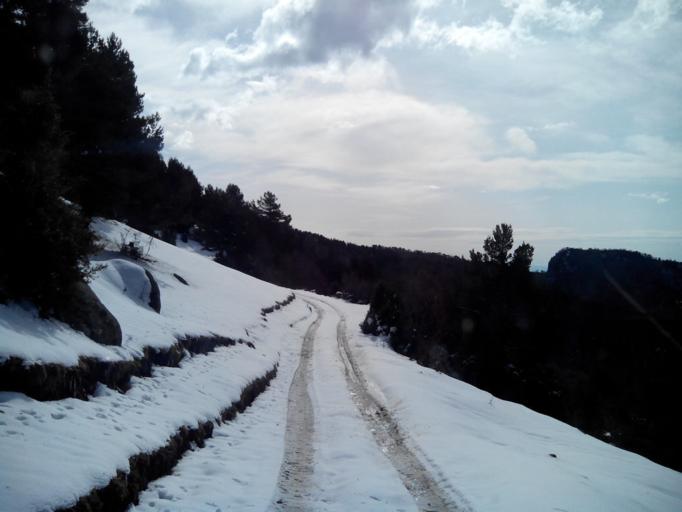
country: ES
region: Catalonia
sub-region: Provincia de Barcelona
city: Sant Julia de Cerdanyola
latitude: 42.1987
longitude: 1.9403
